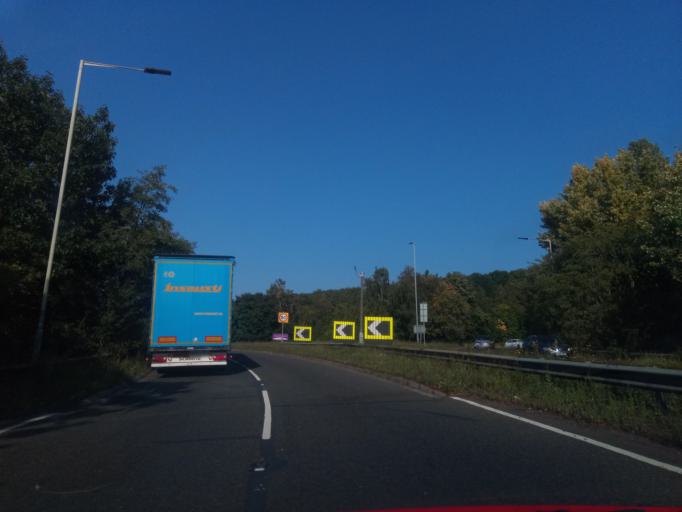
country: GB
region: England
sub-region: Rotherham
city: Catcliffe
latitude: 53.4052
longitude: -1.3498
